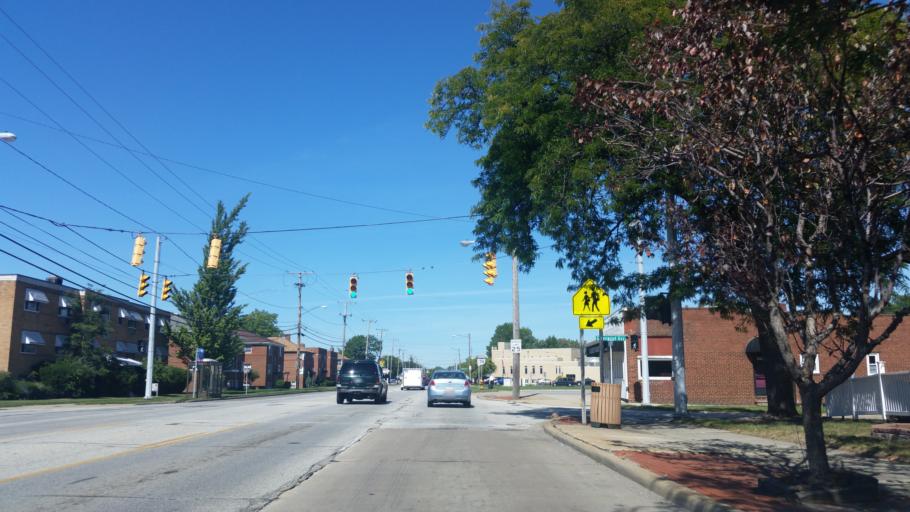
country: US
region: Ohio
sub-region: Cuyahoga County
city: Brooklyn Heights
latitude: 41.4133
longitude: -81.6934
